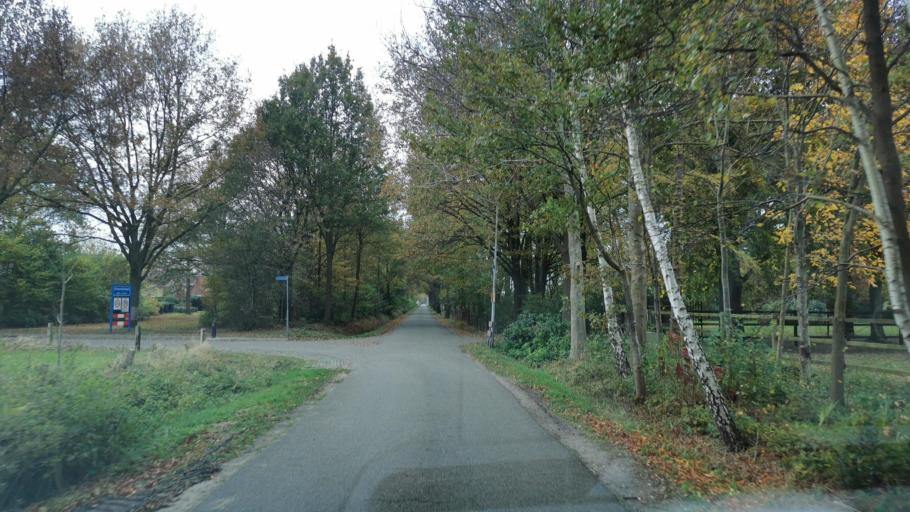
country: DE
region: North Rhine-Westphalia
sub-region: Regierungsbezirk Munster
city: Gronau
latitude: 52.2367
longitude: 7.0471
